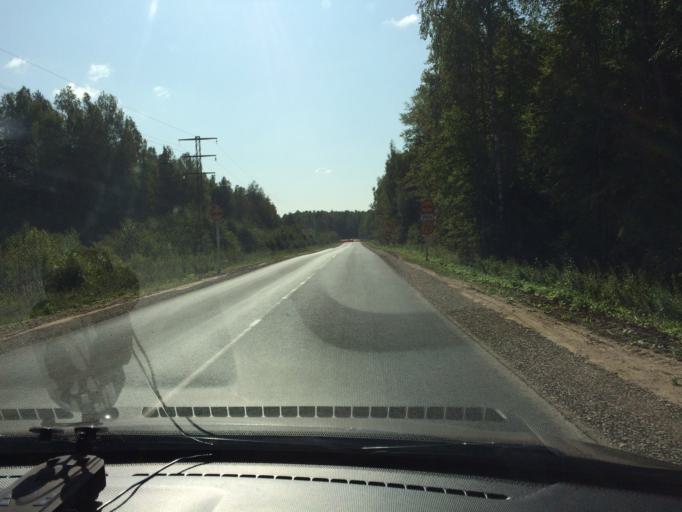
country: RU
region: Mariy-El
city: Surok
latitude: 56.5536
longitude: 48.3135
